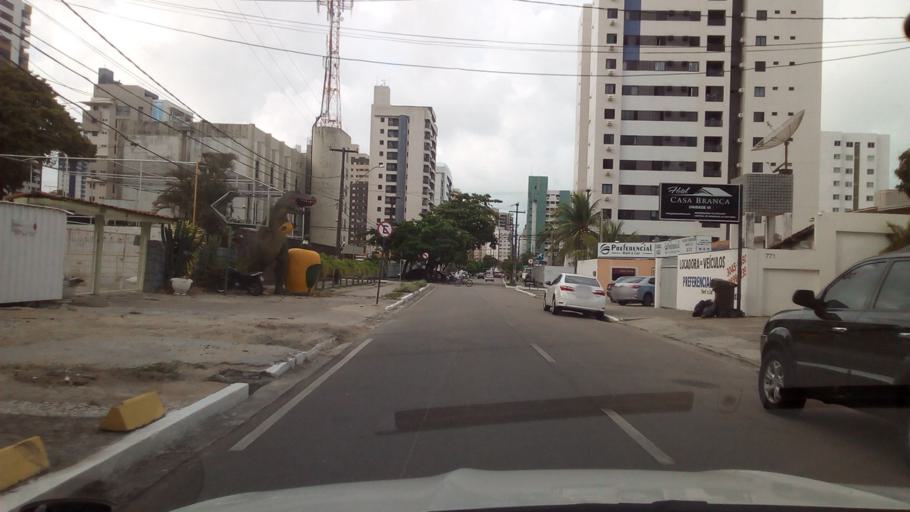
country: BR
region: Paraiba
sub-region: Joao Pessoa
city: Joao Pessoa
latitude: -7.1185
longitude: -34.8273
